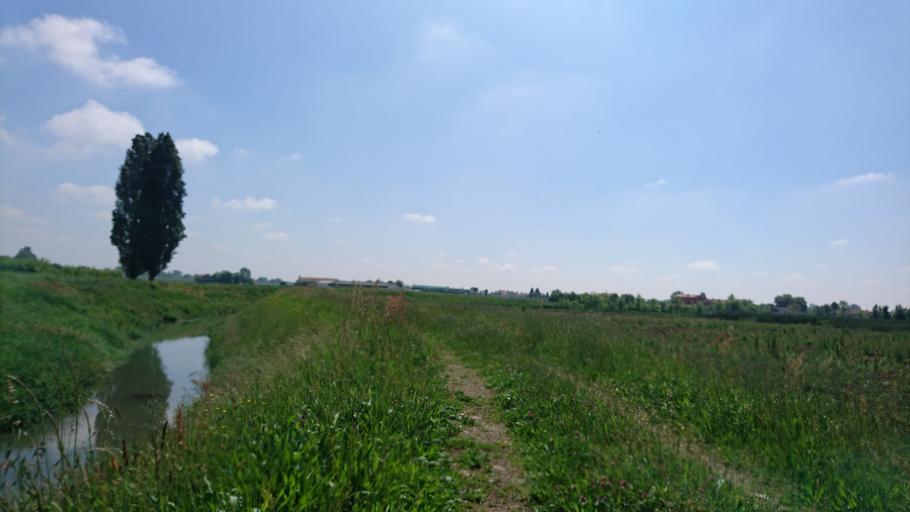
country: IT
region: Veneto
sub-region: Provincia di Padova
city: Casalserugo
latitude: 45.3341
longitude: 11.9253
